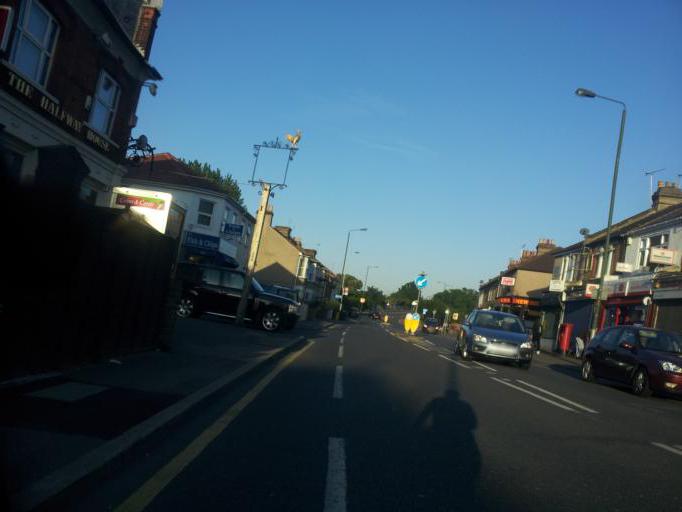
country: GB
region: England
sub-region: Greater London
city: Belvedere
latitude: 51.4903
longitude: 0.1618
